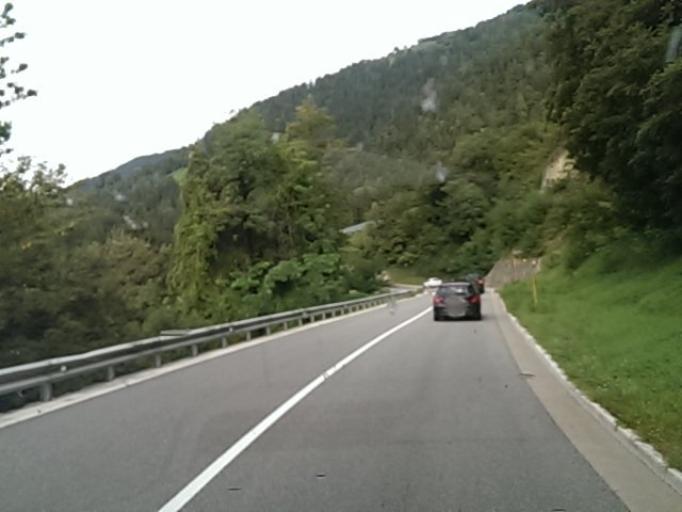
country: IT
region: Trentino-Alto Adige
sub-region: Bolzano
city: San Pancrazio
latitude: 46.6059
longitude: 11.1093
